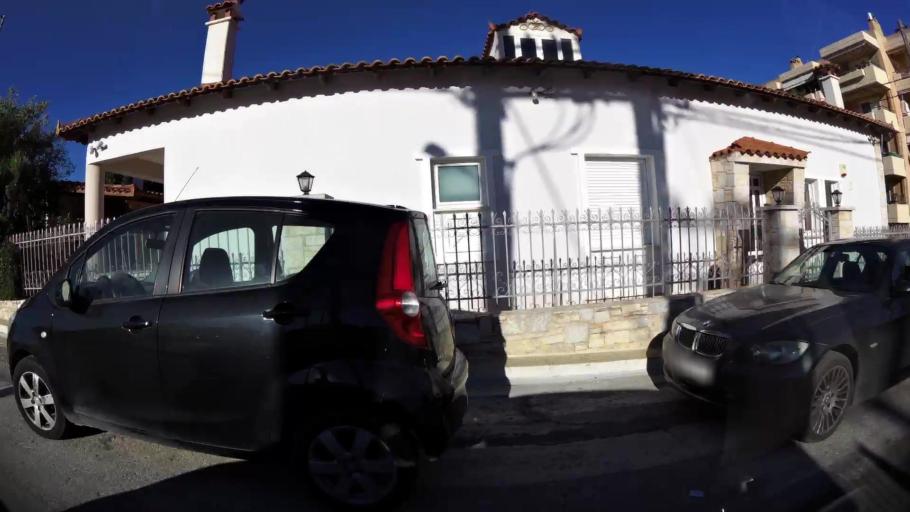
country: GR
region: Attica
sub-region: Nomarchia Anatolikis Attikis
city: Koropi
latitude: 37.8954
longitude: 23.8656
